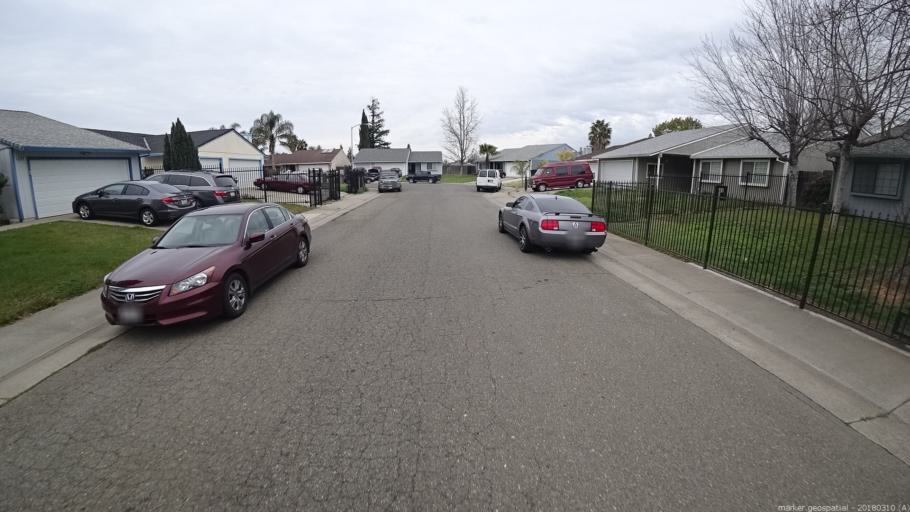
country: US
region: California
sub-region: Sacramento County
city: Vineyard
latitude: 38.4772
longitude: -121.3793
